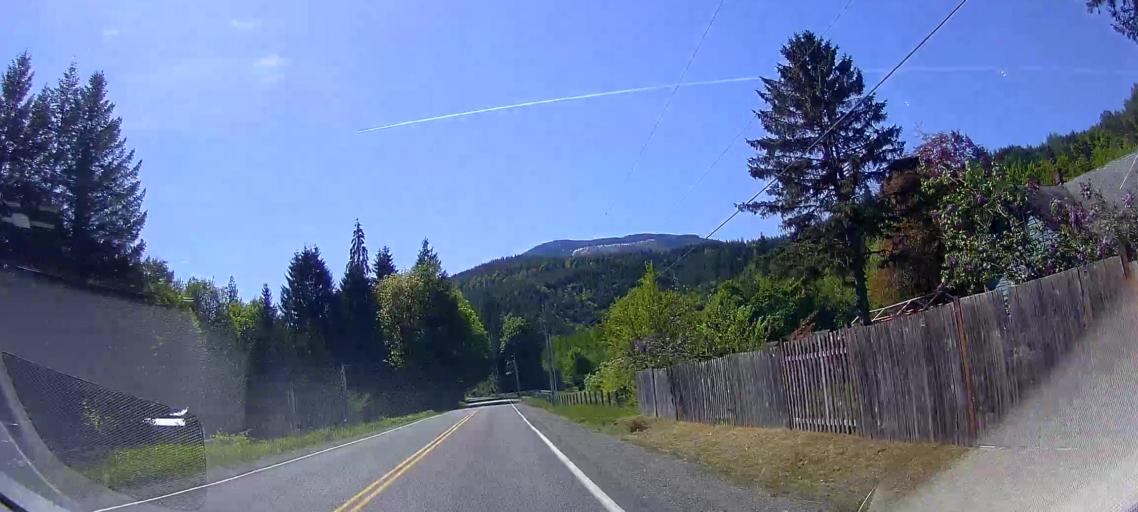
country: US
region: Washington
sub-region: Snohomish County
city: Darrington
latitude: 48.4879
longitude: -121.6550
